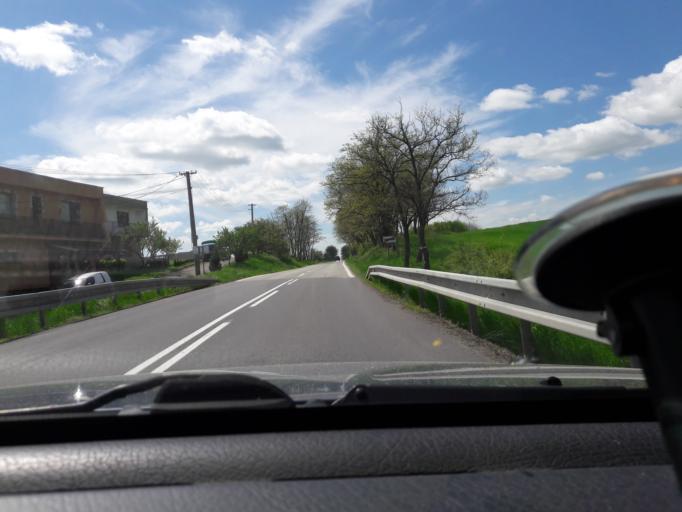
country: SK
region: Banskobystricky
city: Dudince
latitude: 48.2734
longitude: 18.9454
